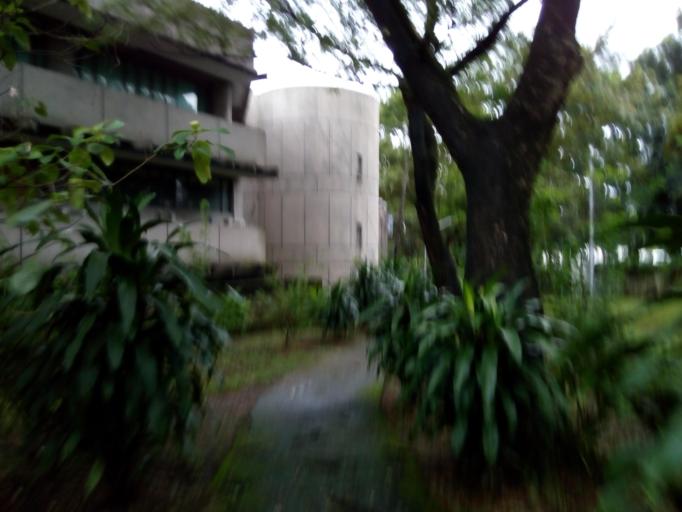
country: PH
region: Metro Manila
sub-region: Quezon City
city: Quezon City
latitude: 14.6491
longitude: 121.0691
